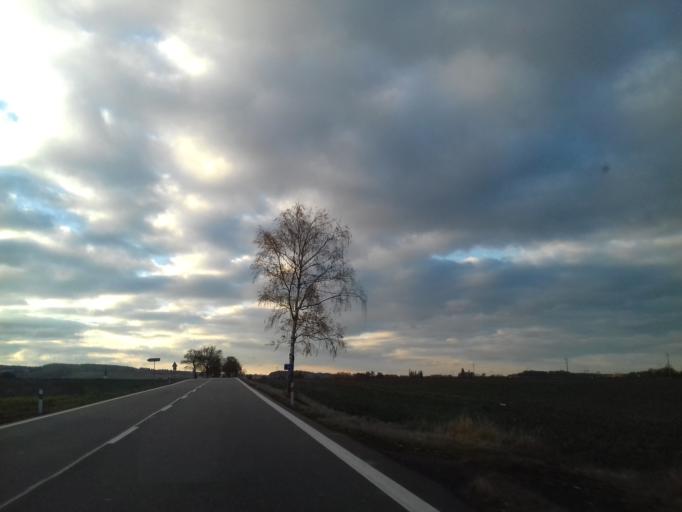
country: CZ
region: Pardubicky
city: Krouna
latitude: 49.7699
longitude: 16.0478
